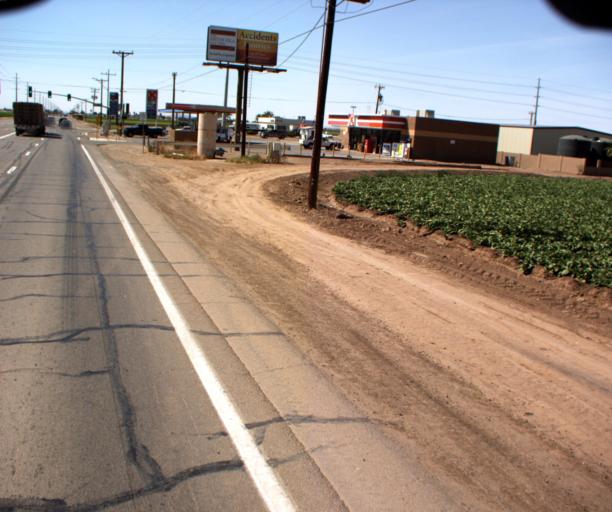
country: US
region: Arizona
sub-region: Yuma County
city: Fortuna Foothills
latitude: 32.6993
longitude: -114.5117
